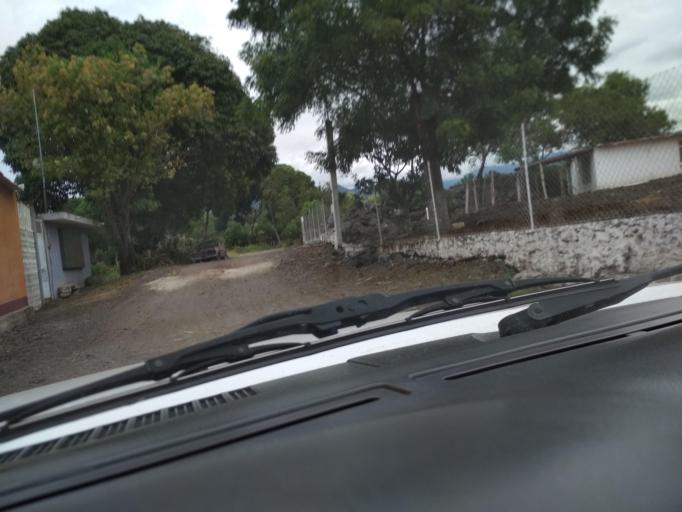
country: MX
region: Veracruz
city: Alto Lucero
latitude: 19.5944
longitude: -96.7836
